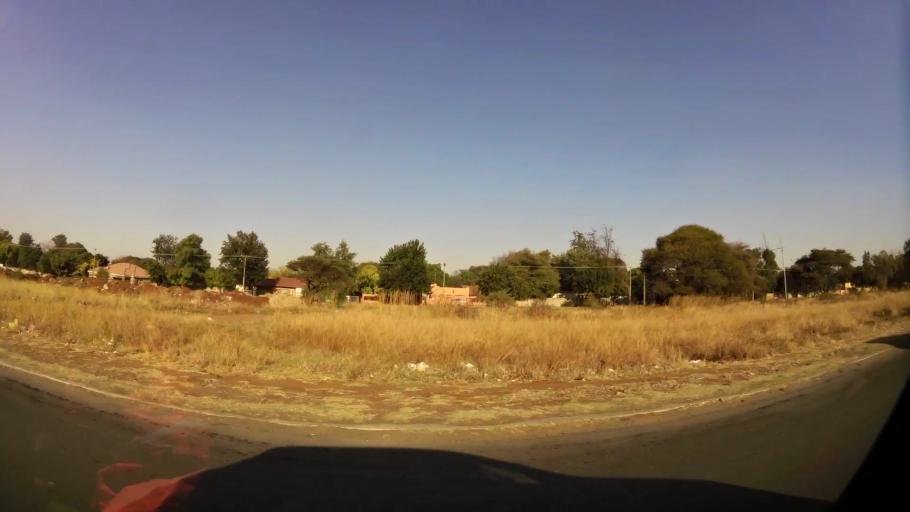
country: ZA
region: North-West
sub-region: Bojanala Platinum District Municipality
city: Rustenburg
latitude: -25.6492
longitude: 27.2247
